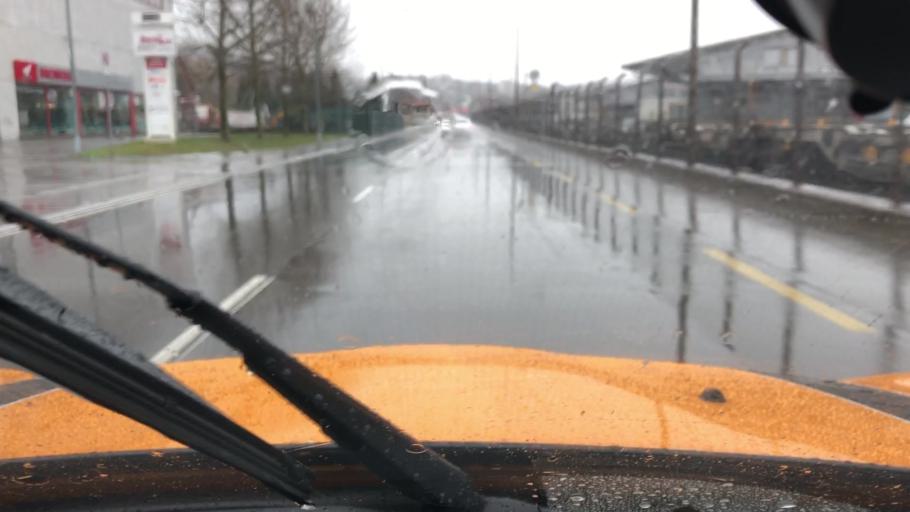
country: CH
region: Ticino
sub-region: Mendrisio District
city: Balerna
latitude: 45.8363
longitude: 9.0115
